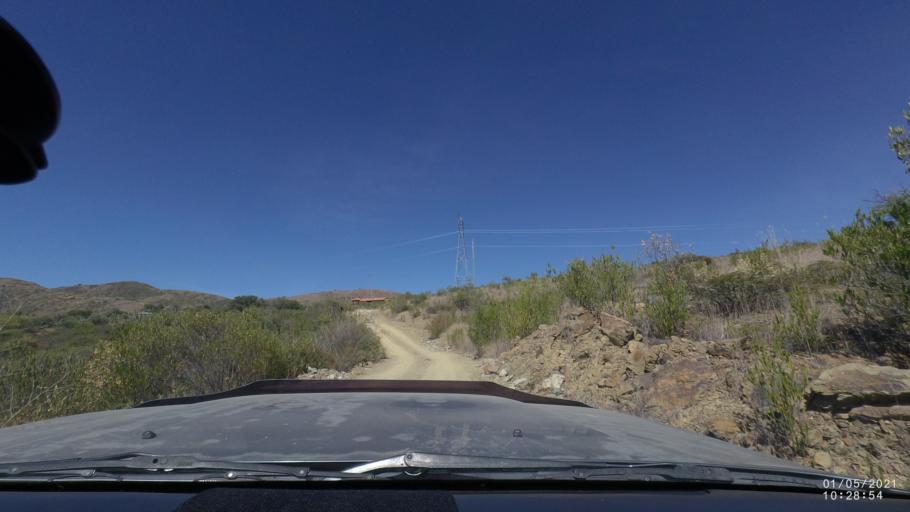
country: BO
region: Cochabamba
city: Capinota
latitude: -17.5910
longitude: -66.1896
